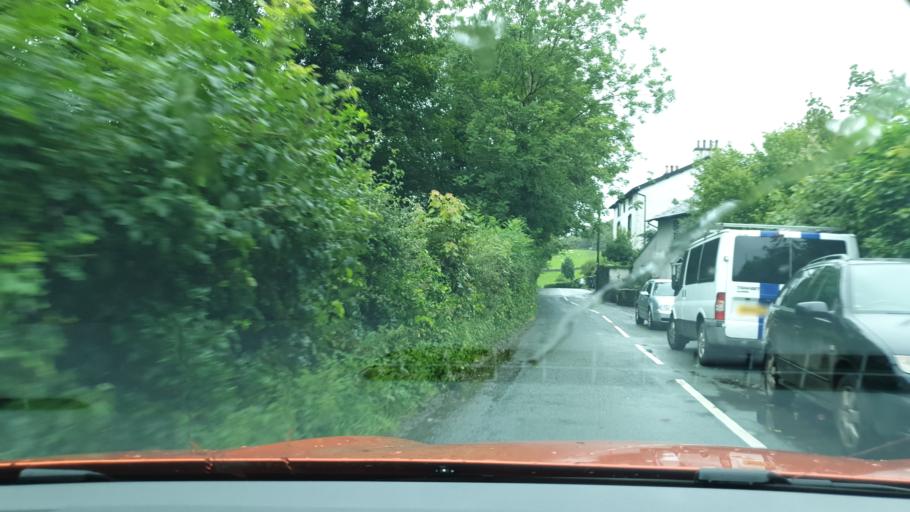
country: GB
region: England
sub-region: Cumbria
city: Ulverston
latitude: 54.2542
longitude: -3.0643
